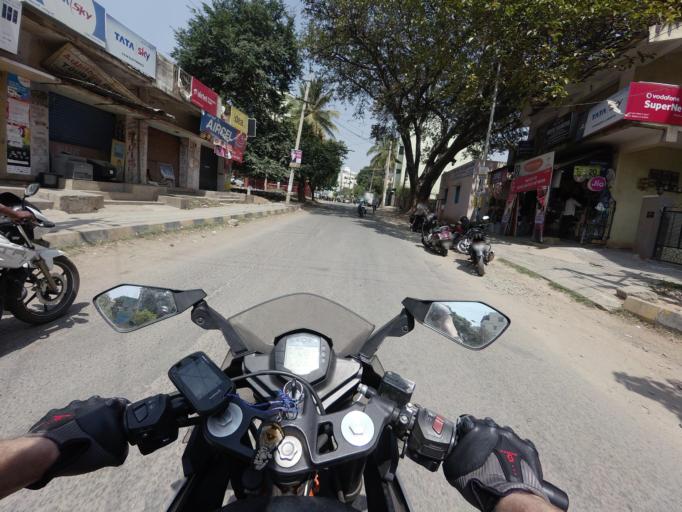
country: IN
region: Karnataka
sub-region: Bangalore Urban
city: Bangalore
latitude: 13.0064
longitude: 77.6454
